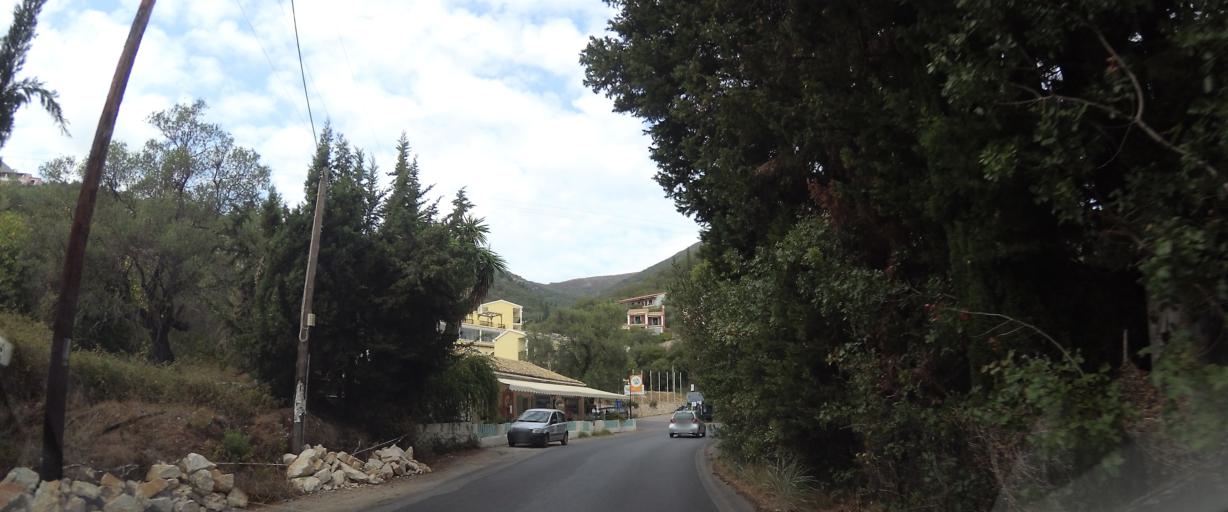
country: GR
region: Ionian Islands
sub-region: Nomos Kerkyras
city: Kontokali
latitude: 39.7251
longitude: 19.8924
